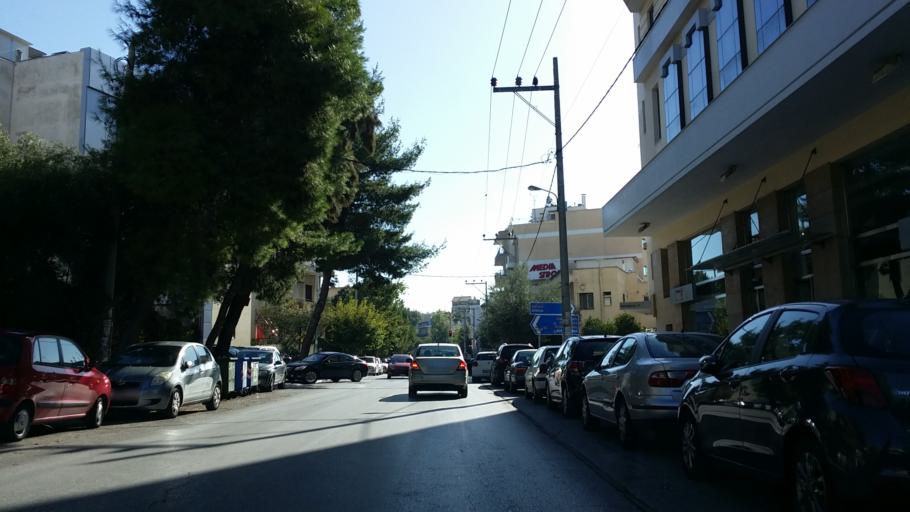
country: GR
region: Attica
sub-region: Nomarchia Athinas
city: Irakleio
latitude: 38.0474
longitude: 23.7578
